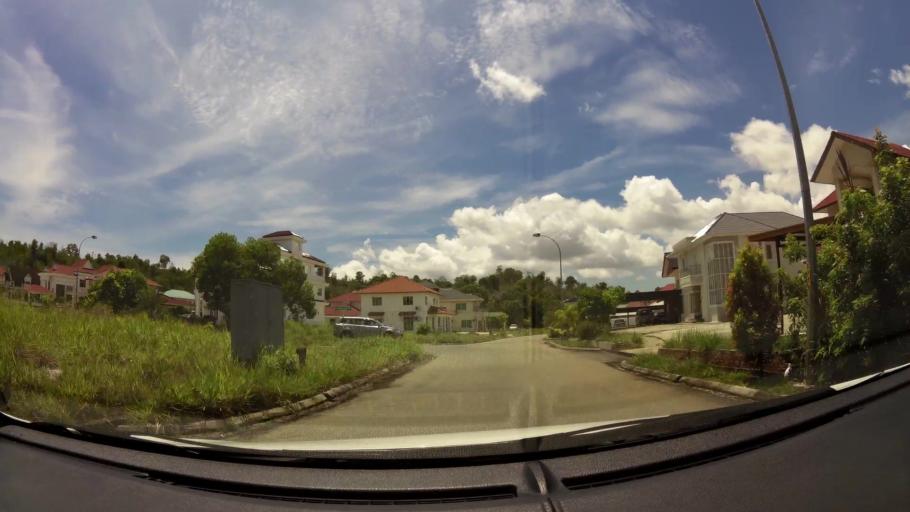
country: BN
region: Brunei and Muara
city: Bandar Seri Begawan
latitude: 4.9720
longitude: 114.9074
